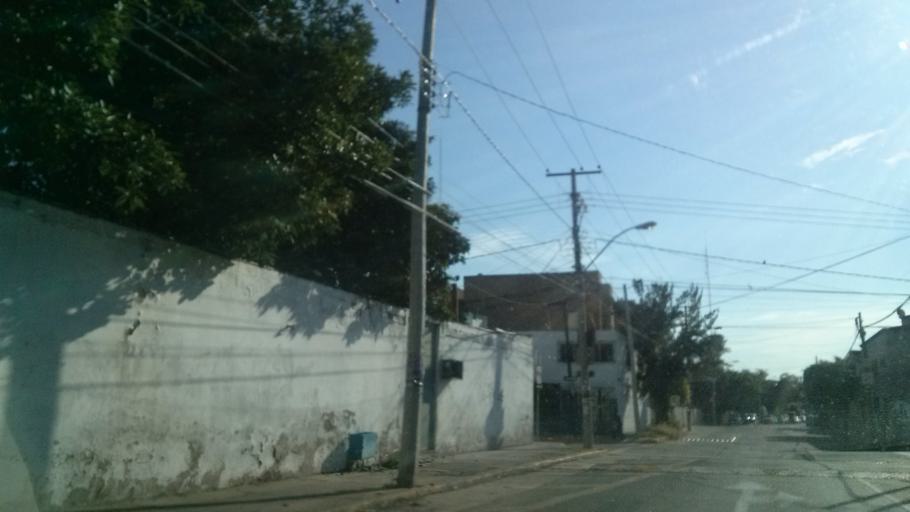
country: MX
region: Guanajuato
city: Leon
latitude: 21.1159
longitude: -101.6649
